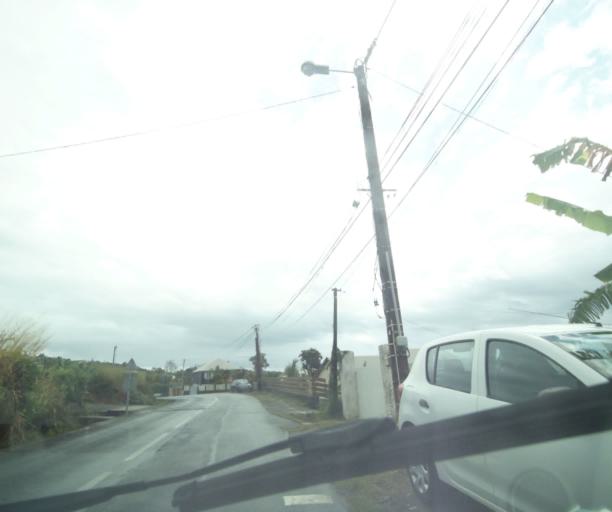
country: RE
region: Reunion
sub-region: Reunion
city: Saint-Paul
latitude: -21.0153
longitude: 55.3068
